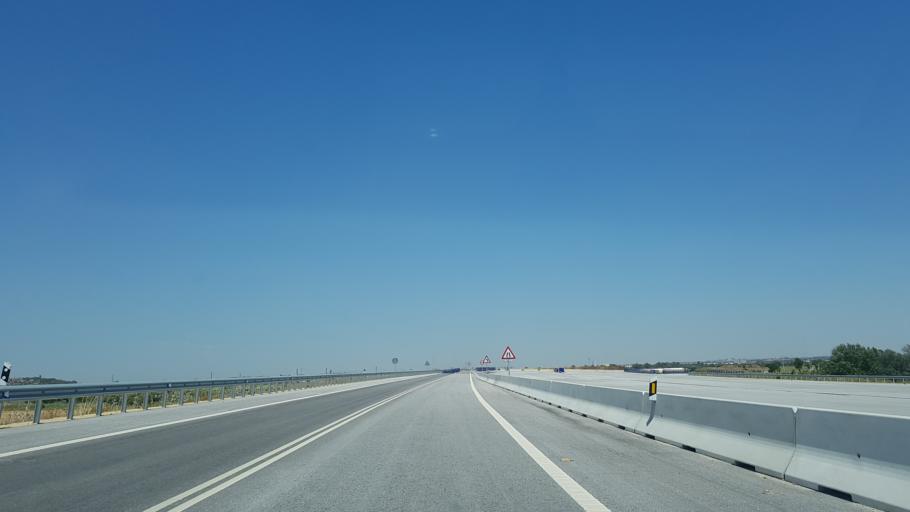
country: ES
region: Andalusia
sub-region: Provincia de Sevilla
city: Coria del Rio
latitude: 37.3049
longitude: -6.0469
